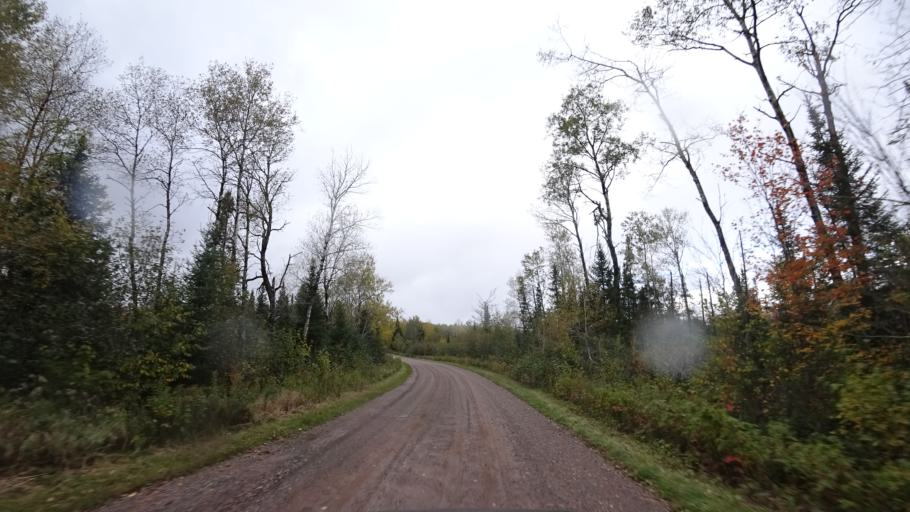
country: US
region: Wisconsin
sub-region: Sawyer County
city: Little Round Lake
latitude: 45.9806
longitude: -90.9966
